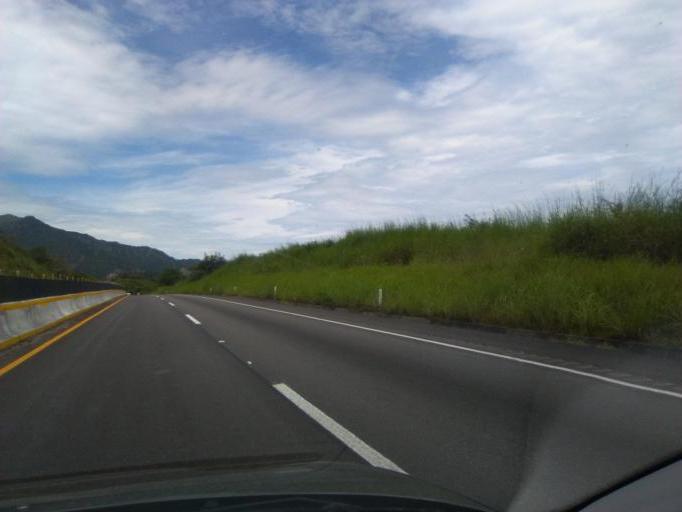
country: MX
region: Guerrero
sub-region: Chilpancingo de los Bravo
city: Cajelitos
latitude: 17.2672
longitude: -99.5124
